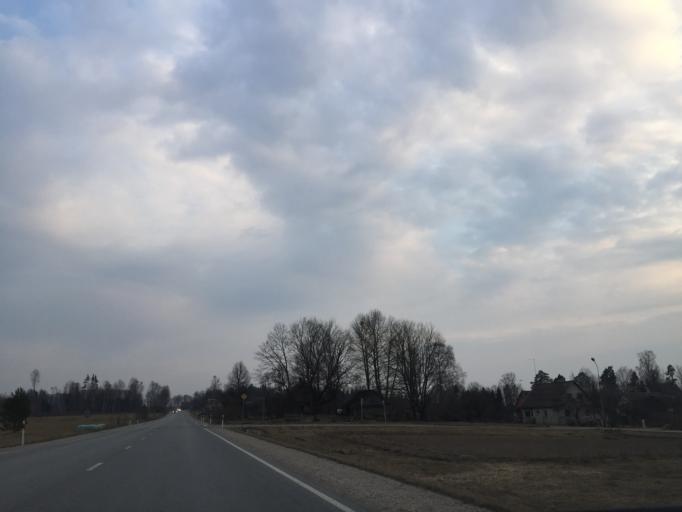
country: LV
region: Vecpiebalga
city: Vecpiebalga
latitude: 57.1545
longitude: 25.6650
